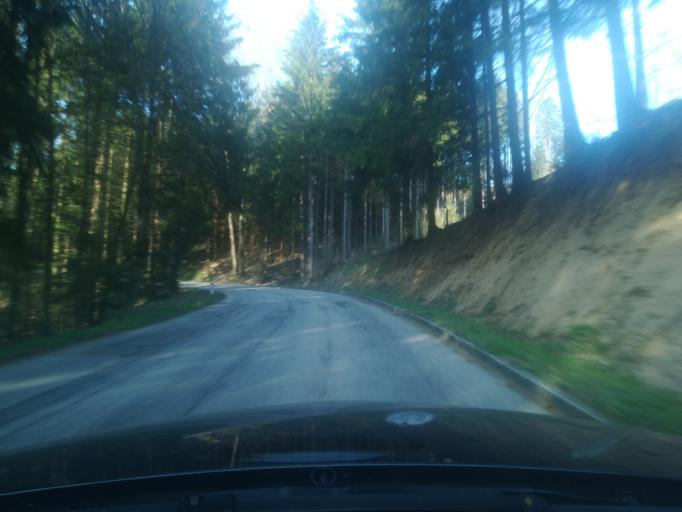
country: AT
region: Upper Austria
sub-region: Politischer Bezirk Perg
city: Bad Kreuzen
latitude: 48.2908
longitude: 14.7747
